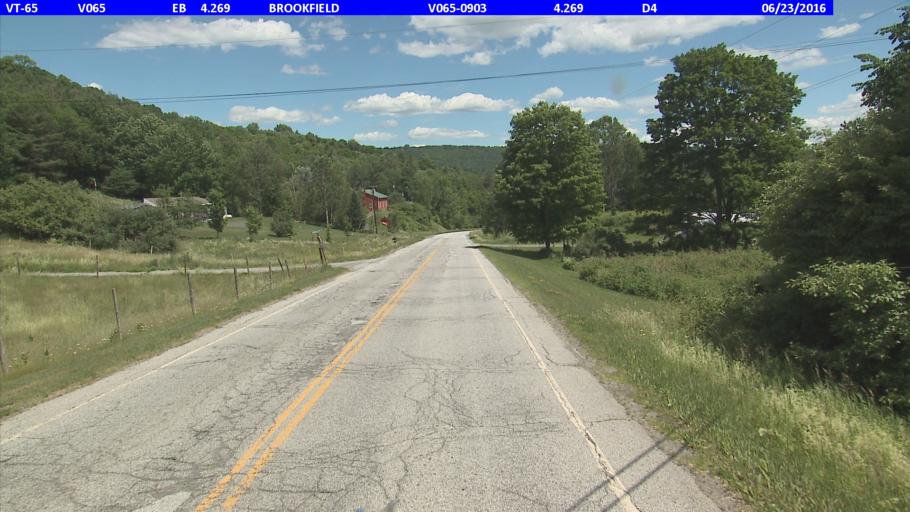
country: US
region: Vermont
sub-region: Orange County
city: Williamstown
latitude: 44.0307
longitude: -72.5870
